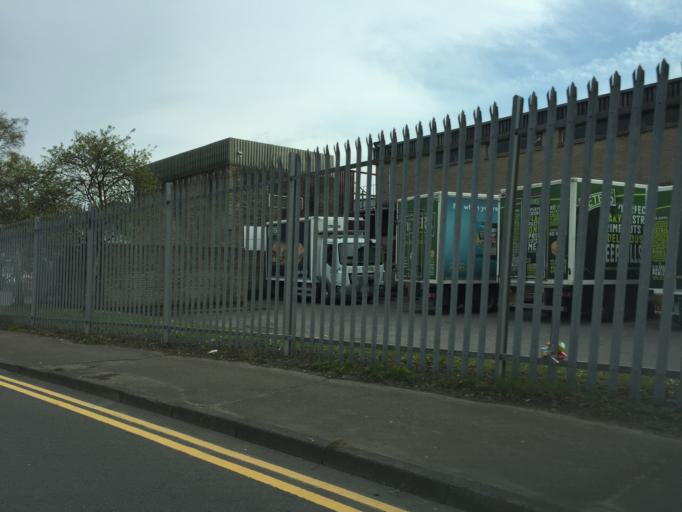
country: GB
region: Wales
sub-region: Caerphilly County Borough
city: Bedwas
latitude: 51.5909
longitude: -3.2053
